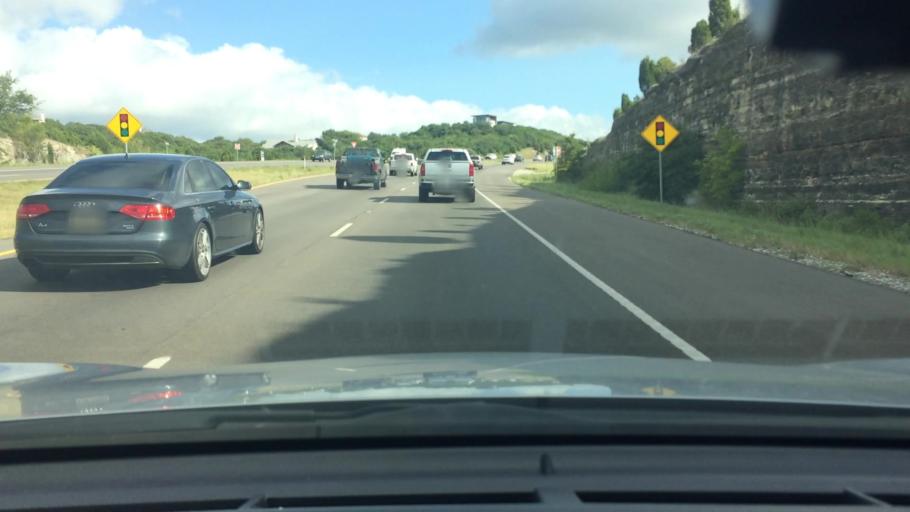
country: US
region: Texas
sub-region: Travis County
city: Lost Creek
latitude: 30.3111
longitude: -97.8264
